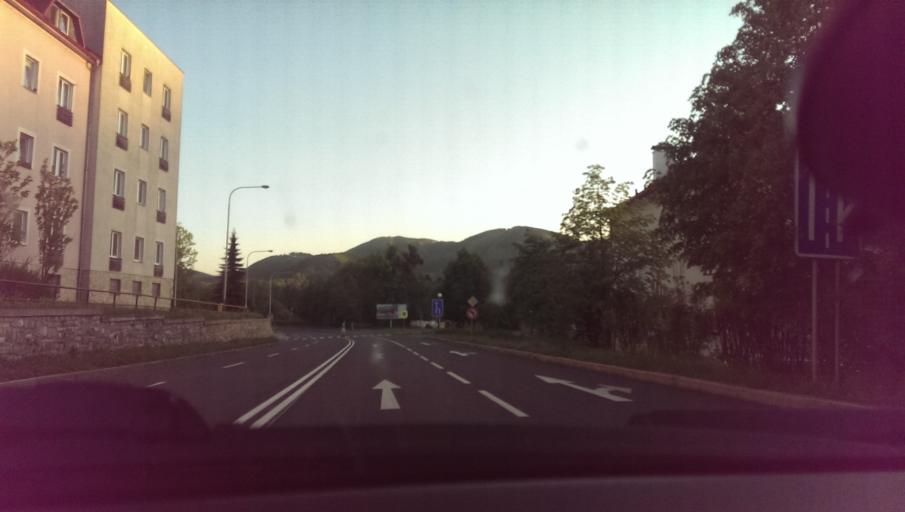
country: CZ
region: Moravskoslezsky
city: Frenstat pod Radhostem
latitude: 49.5402
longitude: 18.2056
